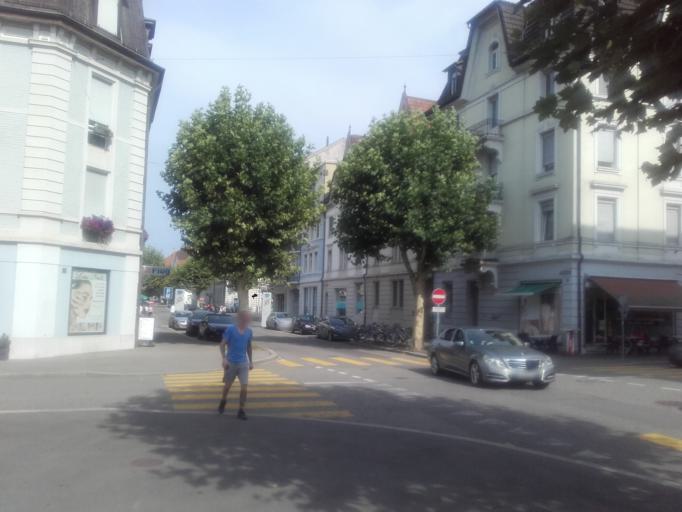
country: CH
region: Solothurn
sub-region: Bezirk Solothurn
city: Solothurn
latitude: 47.2047
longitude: 7.5402
